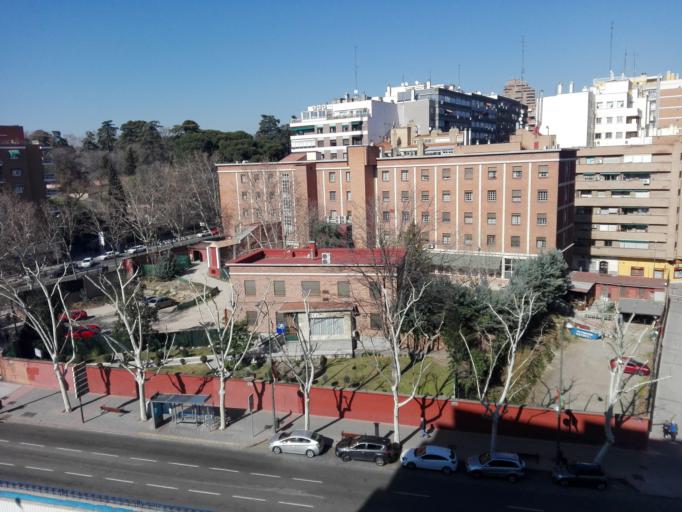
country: ES
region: Madrid
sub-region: Provincia de Madrid
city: Retiro
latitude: 40.4074
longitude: -3.6777
